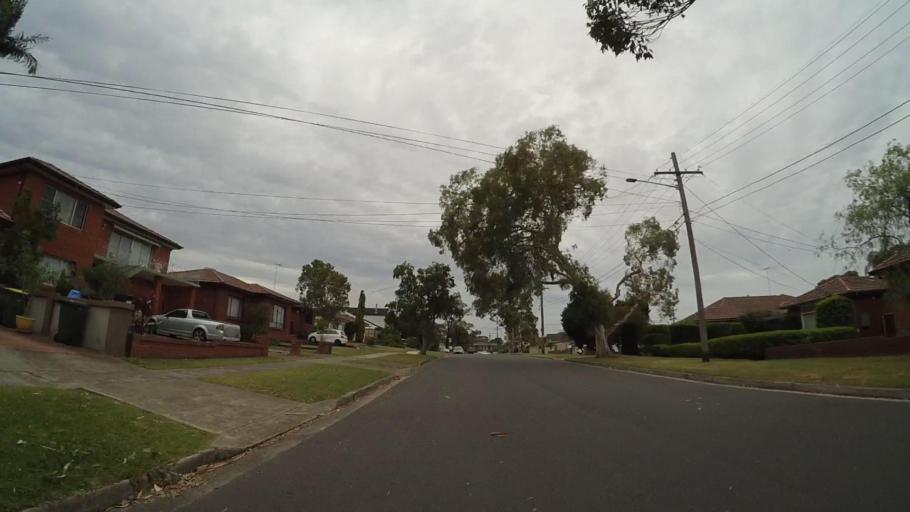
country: AU
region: New South Wales
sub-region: Sutherland Shire
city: Gymea
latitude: -34.0255
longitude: 151.0893
